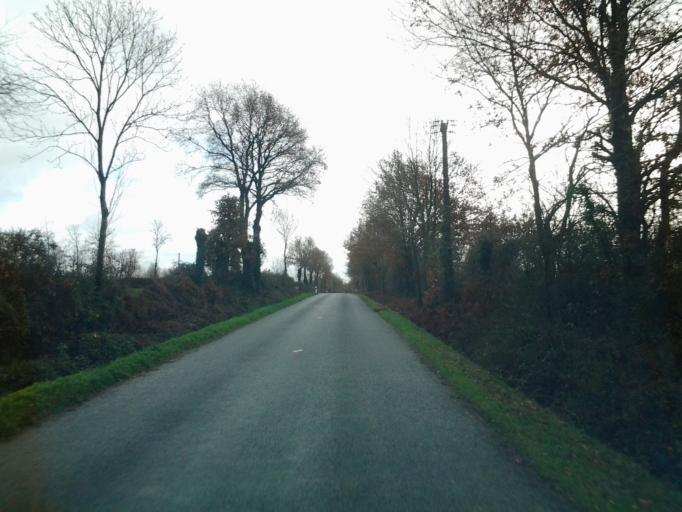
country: FR
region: Pays de la Loire
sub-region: Departement de la Vendee
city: Nesmy
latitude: 46.6430
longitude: -1.3654
